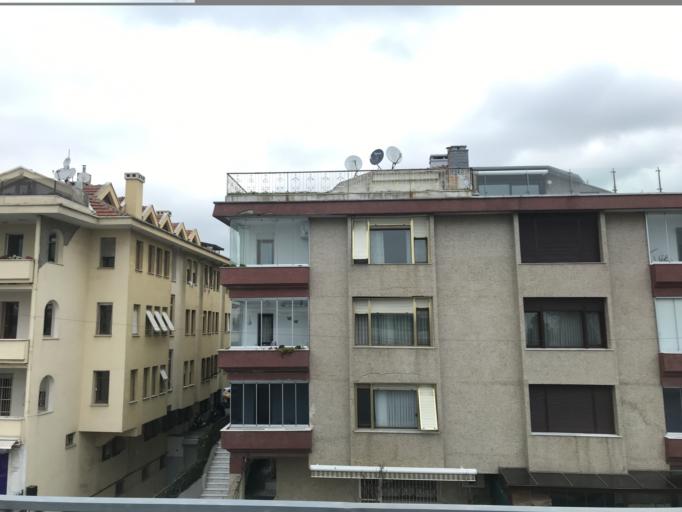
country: TR
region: Istanbul
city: Bahcelievler
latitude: 40.9645
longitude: 28.8036
